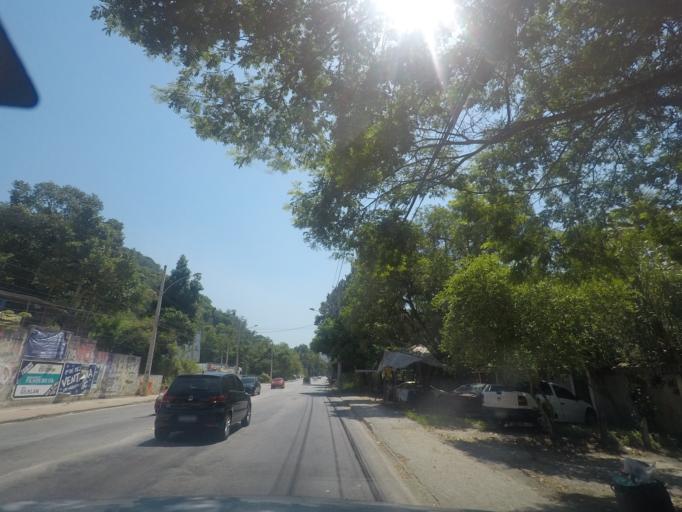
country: BR
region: Rio de Janeiro
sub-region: Nilopolis
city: Nilopolis
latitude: -22.9880
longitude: -43.4816
